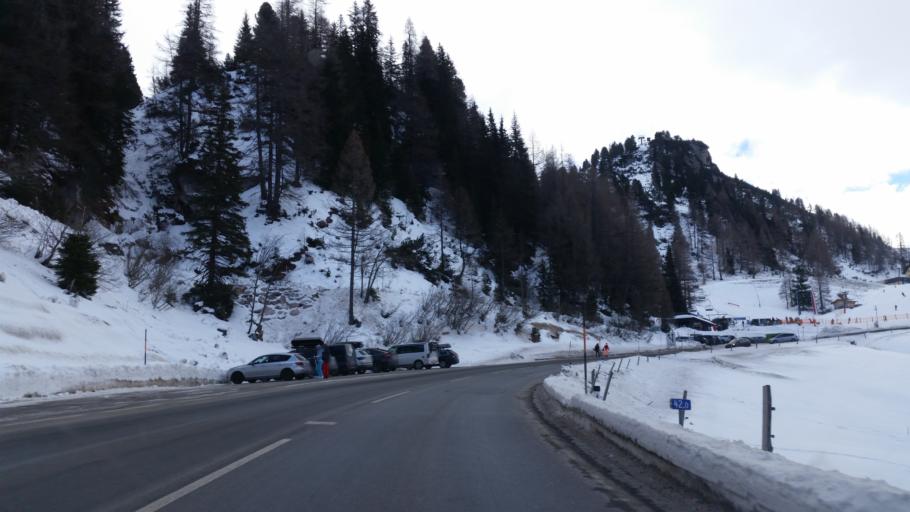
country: AT
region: Salzburg
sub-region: Politischer Bezirk Sankt Johann im Pongau
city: Untertauern
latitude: 47.2547
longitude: 13.5244
